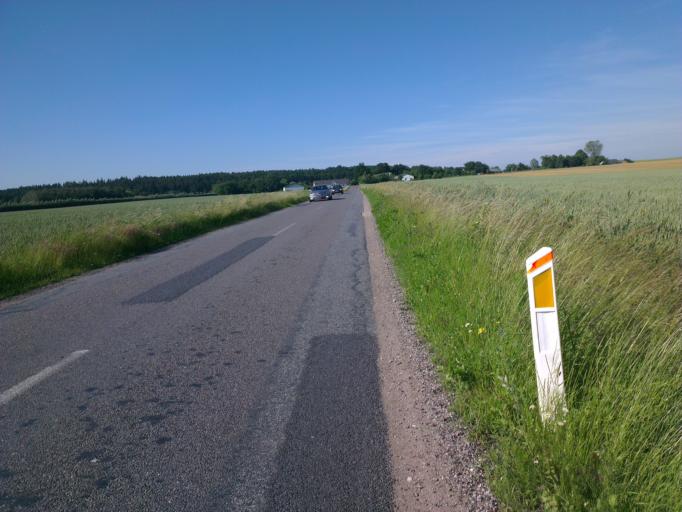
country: DK
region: Capital Region
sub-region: Frederikssund Kommune
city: Skibby
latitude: 55.7991
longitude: 11.9615
